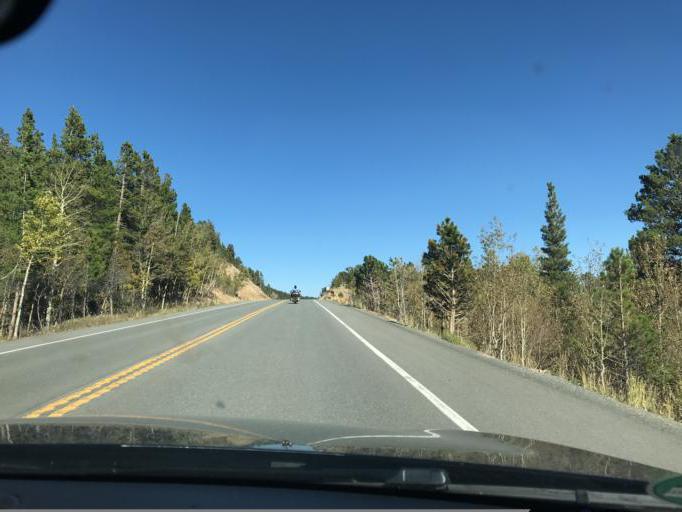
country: US
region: Colorado
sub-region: Boulder County
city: Nederland
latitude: 40.0607
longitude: -105.5213
